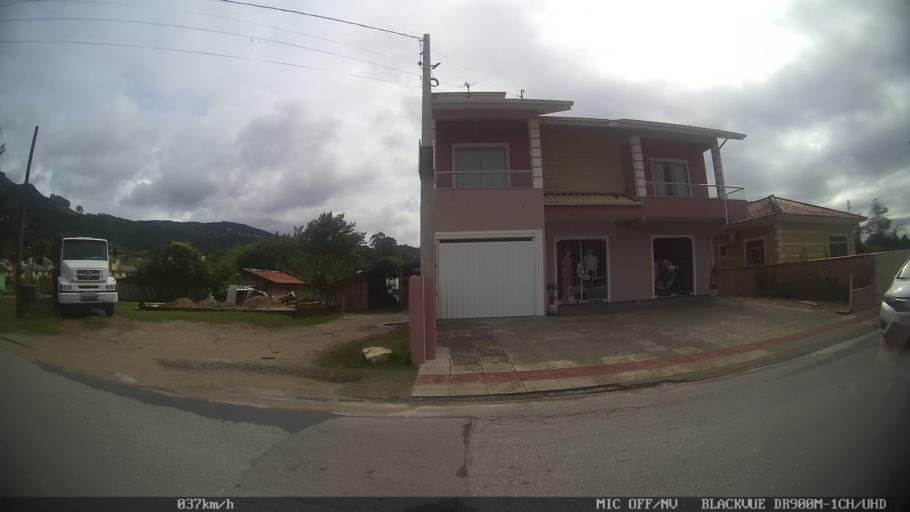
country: BR
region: Santa Catarina
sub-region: Biguacu
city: Biguacu
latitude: -27.5173
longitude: -48.6553
